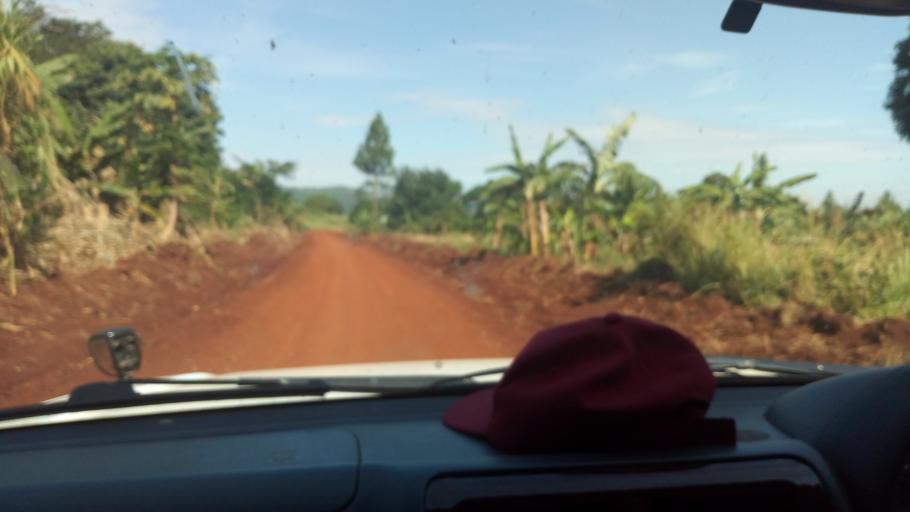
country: UG
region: Western Region
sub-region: Masindi District
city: Masindi
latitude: 1.6435
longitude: 31.7696
